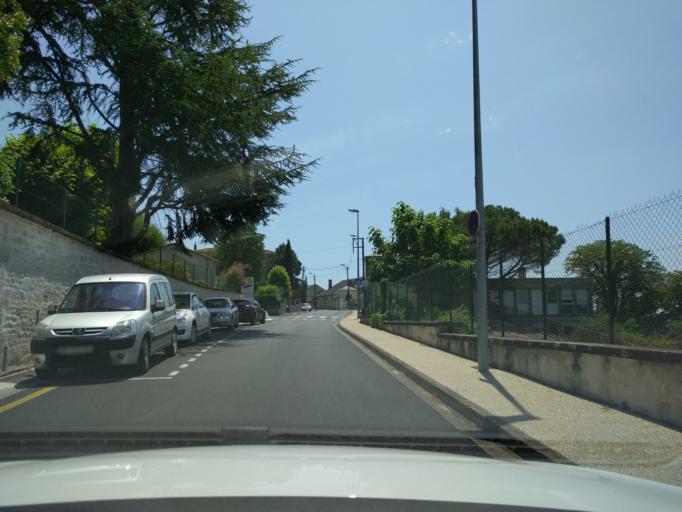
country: FR
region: Poitou-Charentes
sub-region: Departement des Deux-Sevres
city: Niort
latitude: 46.3343
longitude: -0.4618
